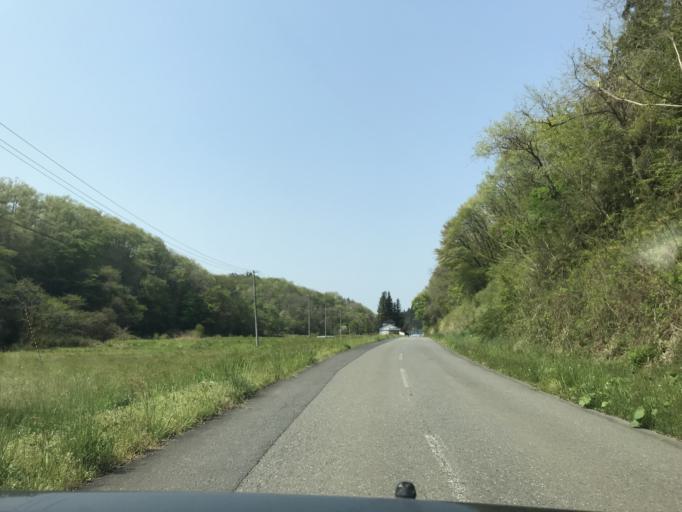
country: JP
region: Iwate
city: Ichinoseki
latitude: 38.8964
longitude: 141.0826
